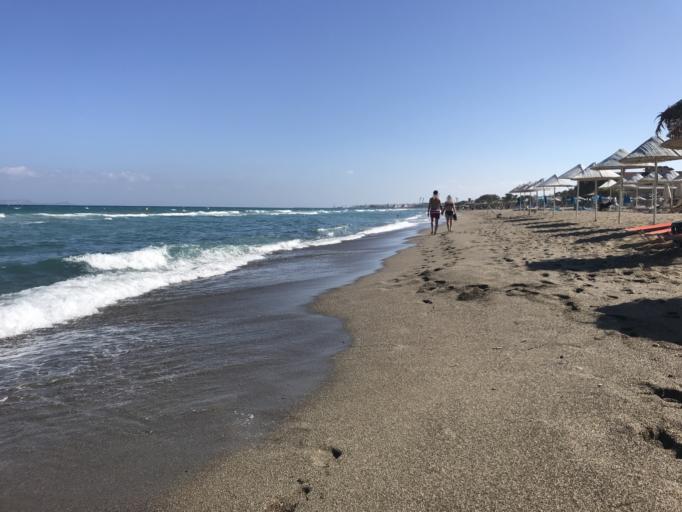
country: GR
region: Crete
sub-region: Nomos Irakleiou
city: Gazi
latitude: 35.3381
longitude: 25.0745
